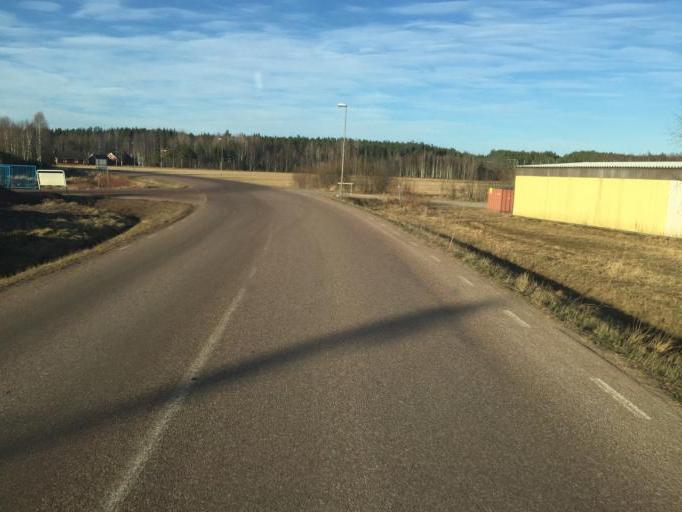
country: SE
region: Dalarna
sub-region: Gagnefs Kommun
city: Mockfjard
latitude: 60.4976
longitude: 14.9747
